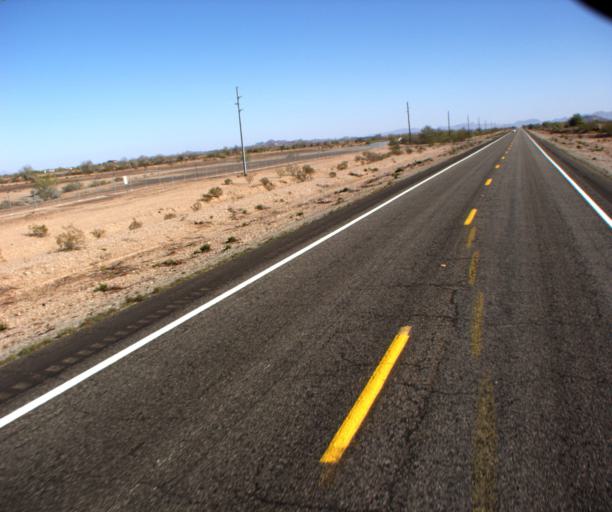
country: US
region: Arizona
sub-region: Yuma County
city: Fortuna Foothills
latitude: 32.8778
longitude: -114.3487
